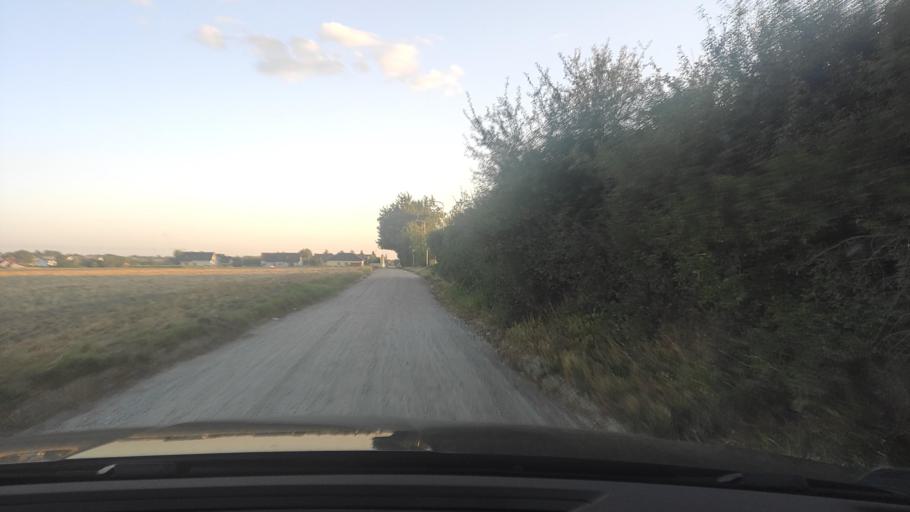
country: PL
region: Greater Poland Voivodeship
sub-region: Powiat poznanski
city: Swarzedz
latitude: 52.4340
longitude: 17.1167
